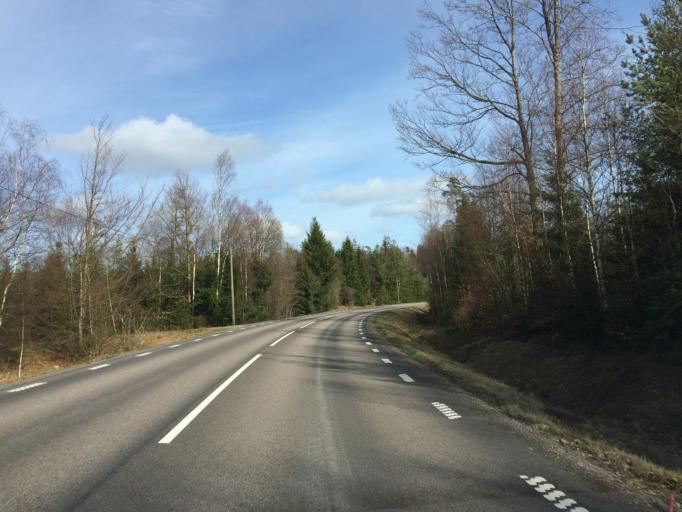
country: SE
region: Halland
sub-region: Hylte Kommun
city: Torup
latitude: 57.0247
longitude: 13.1489
